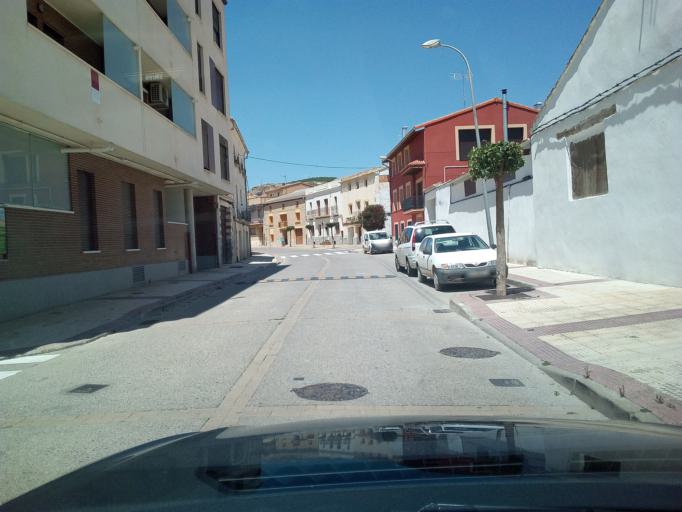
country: ES
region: Navarre
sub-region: Provincia de Navarra
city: Arguedas
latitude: 42.1746
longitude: -1.5955
